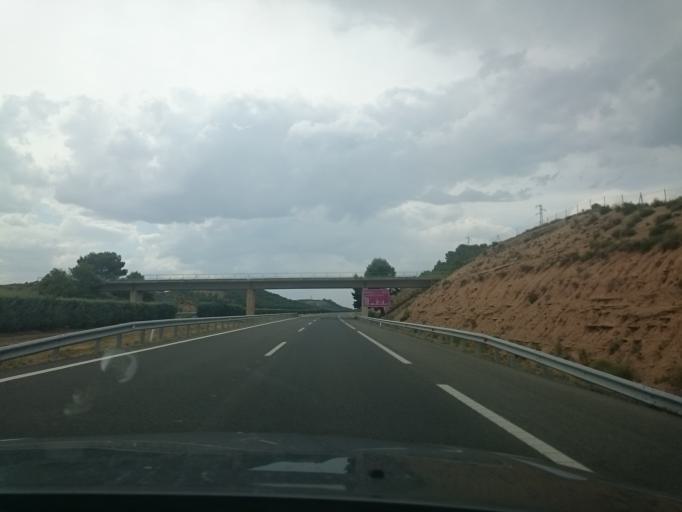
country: ES
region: Navarre
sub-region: Provincia de Navarra
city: Murchante
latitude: 42.0780
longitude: -1.7019
